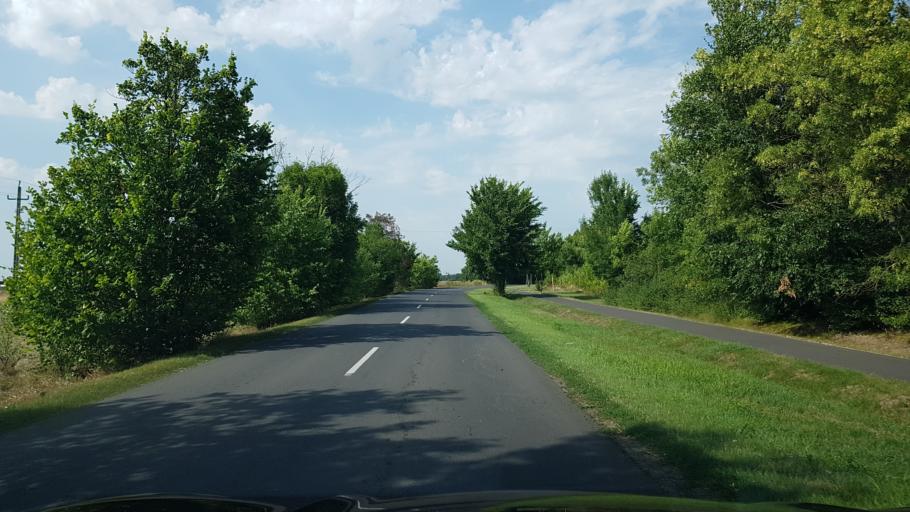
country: HU
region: Bekes
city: Fuzesgyarmat
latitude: 47.0651
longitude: 21.1956
